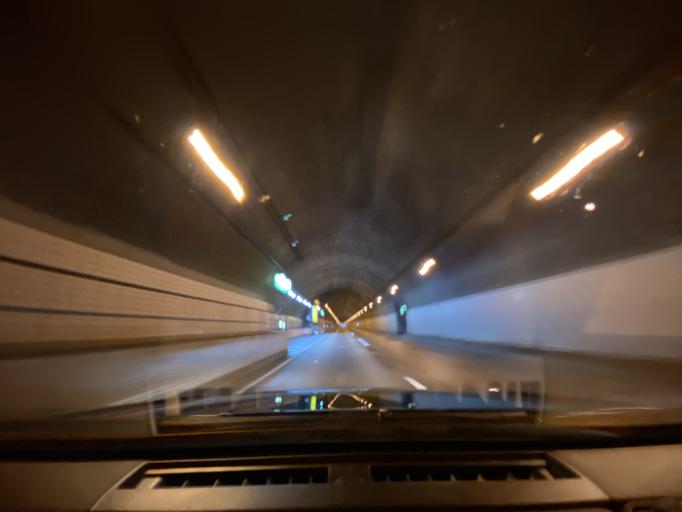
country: JP
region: Hokkaido
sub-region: Asahikawa-shi
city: Asahikawa
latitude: 43.7819
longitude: 142.2242
